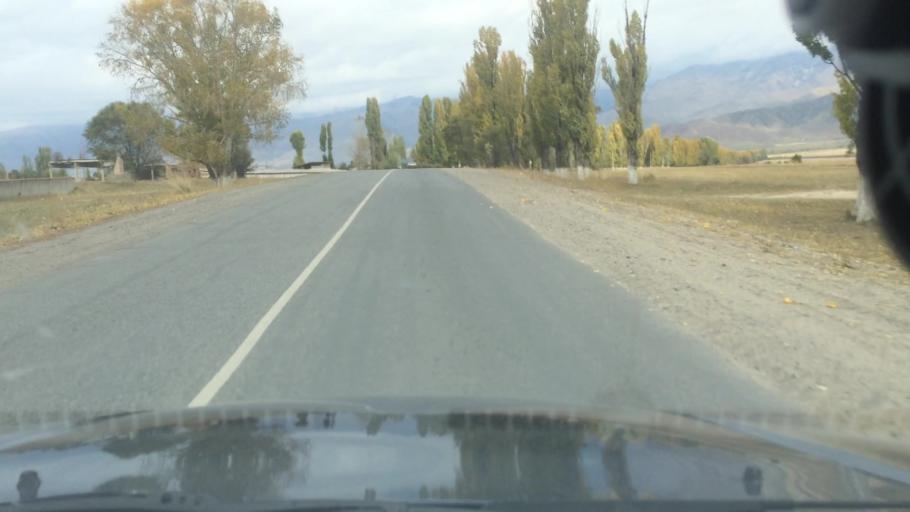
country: KG
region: Ysyk-Koel
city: Tyup
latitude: 42.7416
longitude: 78.3414
